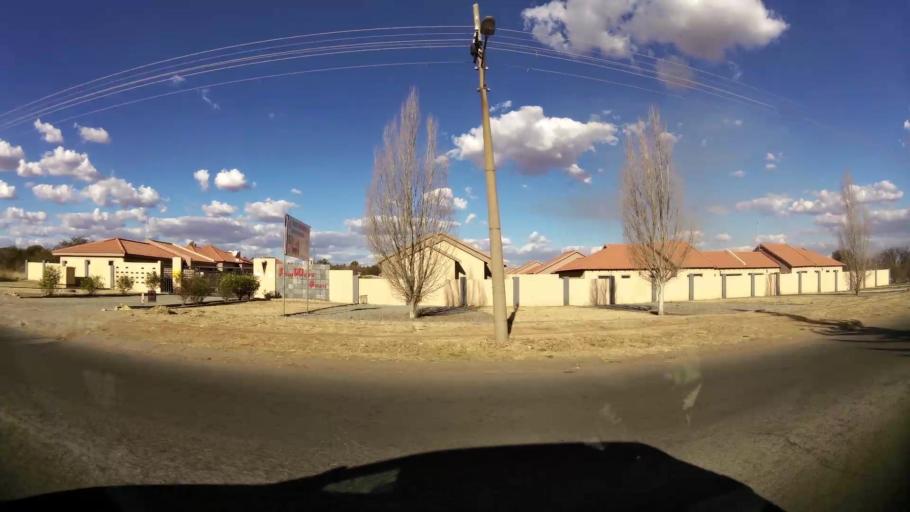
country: ZA
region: North-West
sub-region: Dr Kenneth Kaunda District Municipality
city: Klerksdorp
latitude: -26.8319
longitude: 26.6627
